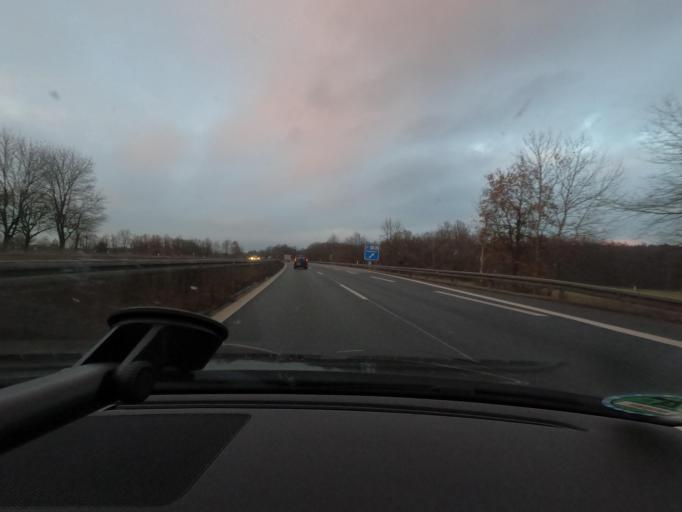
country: DE
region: Bavaria
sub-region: Upper Franconia
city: Eggolsheim
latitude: 49.7514
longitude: 11.0604
